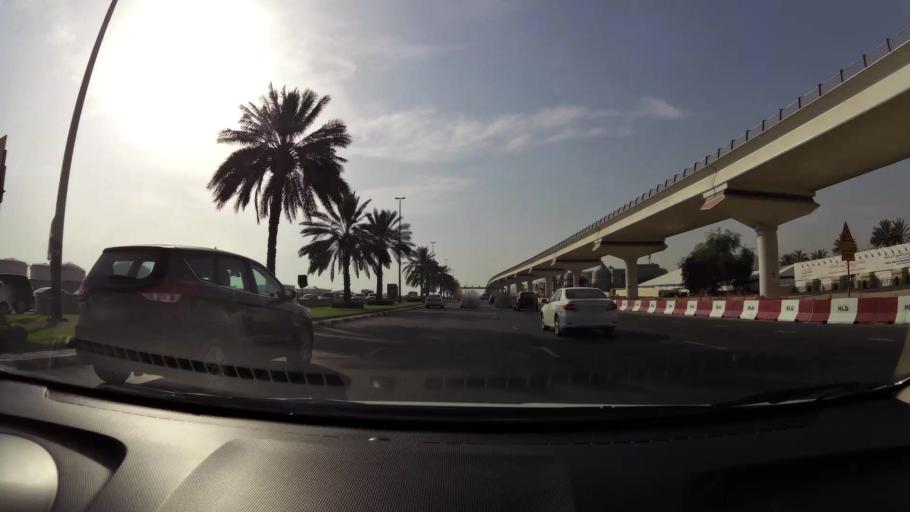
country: AE
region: Ash Shariqah
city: Sharjah
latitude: 25.2344
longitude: 55.3829
